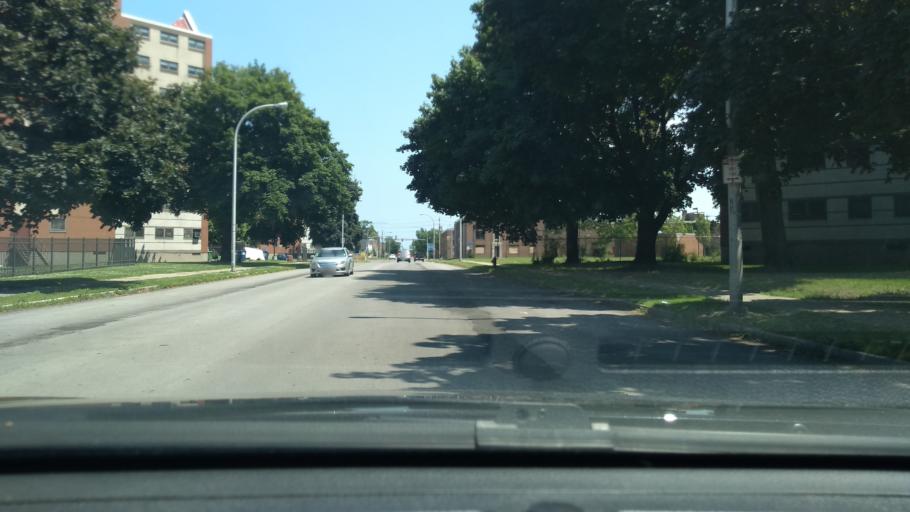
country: US
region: New York
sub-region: Erie County
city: Buffalo
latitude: 42.8741
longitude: -78.8661
